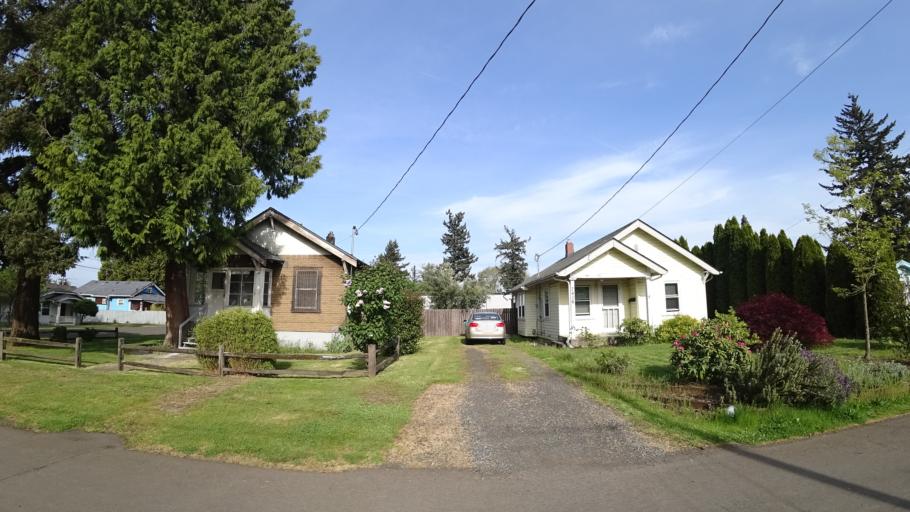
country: US
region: Oregon
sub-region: Clackamas County
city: Milwaukie
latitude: 45.4696
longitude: -122.6110
